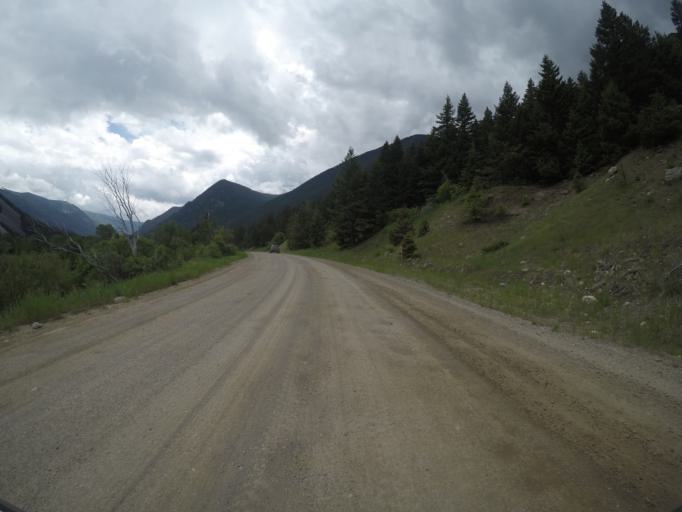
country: US
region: Montana
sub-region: Park County
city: Livingston
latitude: 45.5037
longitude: -110.2274
